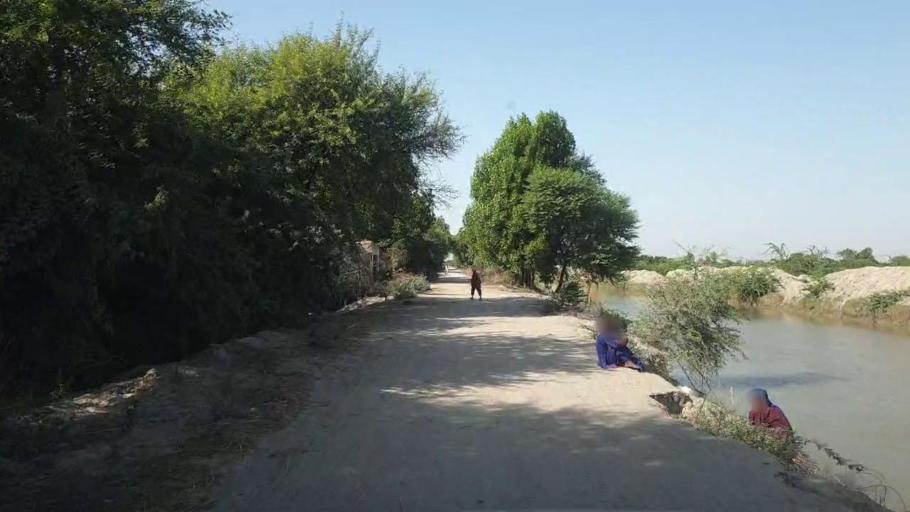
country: PK
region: Sindh
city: Kadhan
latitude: 24.5696
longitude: 68.9888
